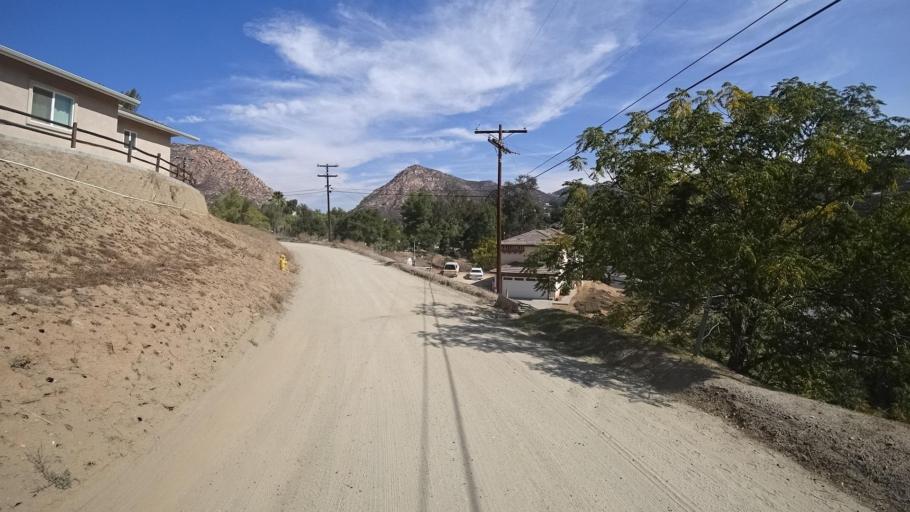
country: US
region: California
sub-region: San Diego County
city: Harbison Canyon
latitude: 32.8190
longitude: -116.8326
